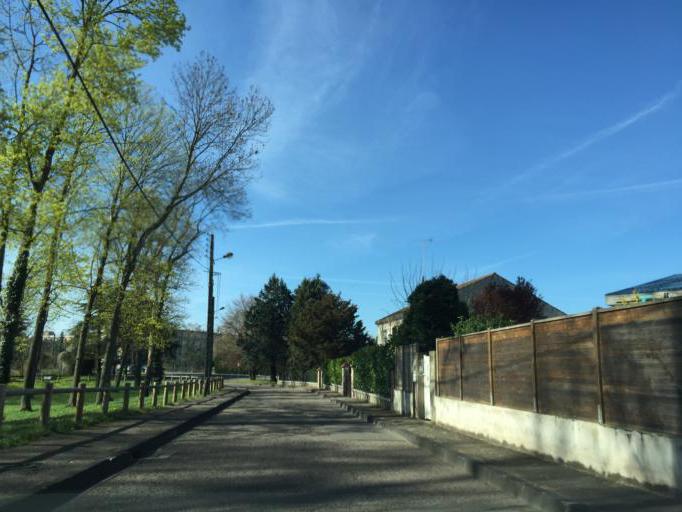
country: FR
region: Rhone-Alpes
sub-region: Departement de la Loire
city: Feurs
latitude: 45.7493
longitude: 4.2226
